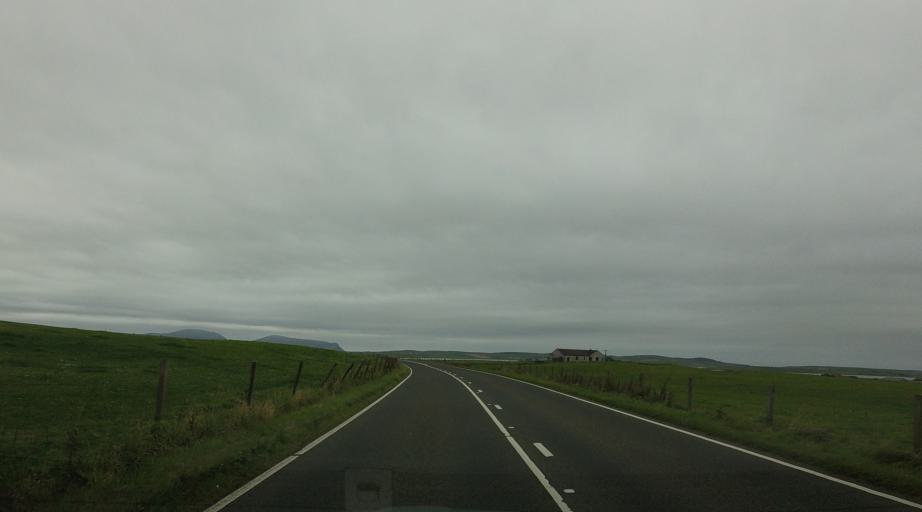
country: GB
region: Scotland
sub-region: Orkney Islands
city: Stromness
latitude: 59.0029
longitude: -3.1703
